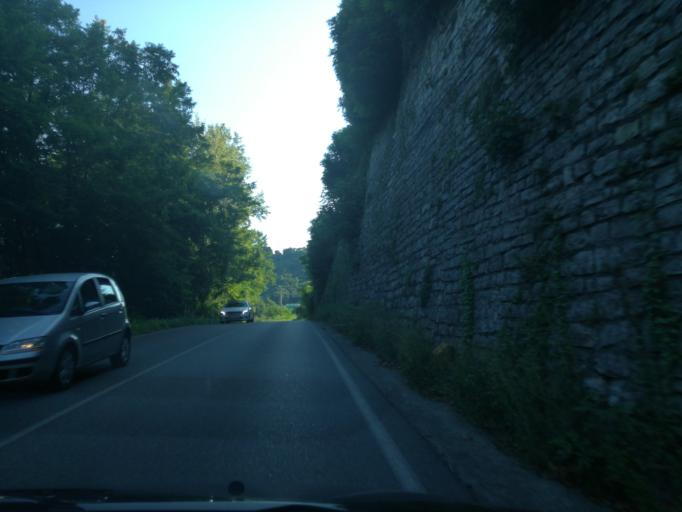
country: IT
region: Lombardy
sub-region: Provincia di Lecco
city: Brivio
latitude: 45.7325
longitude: 9.4428
